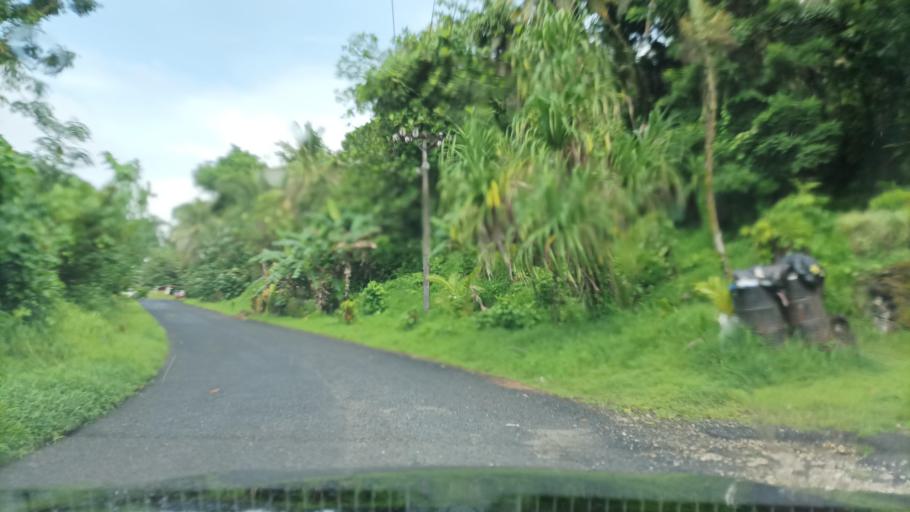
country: FM
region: Pohnpei
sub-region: Madolenihm Municipality
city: Madolenihm Municipality Government
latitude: 6.9201
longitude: 158.3086
